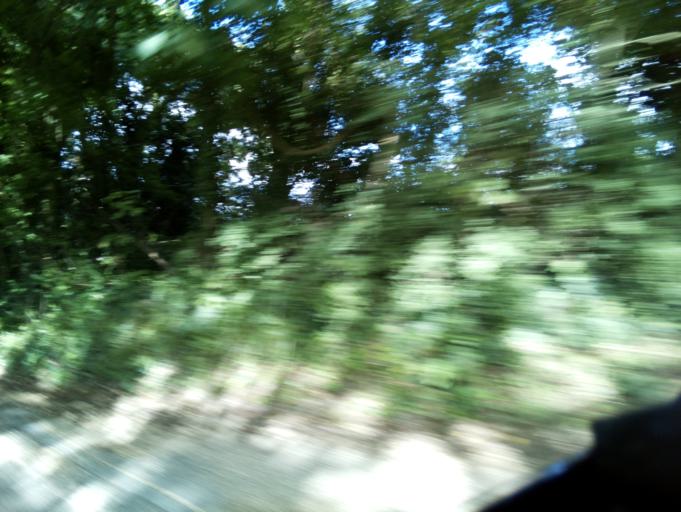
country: GB
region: England
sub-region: Hampshire
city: Winchester
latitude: 51.0828
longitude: -1.3746
